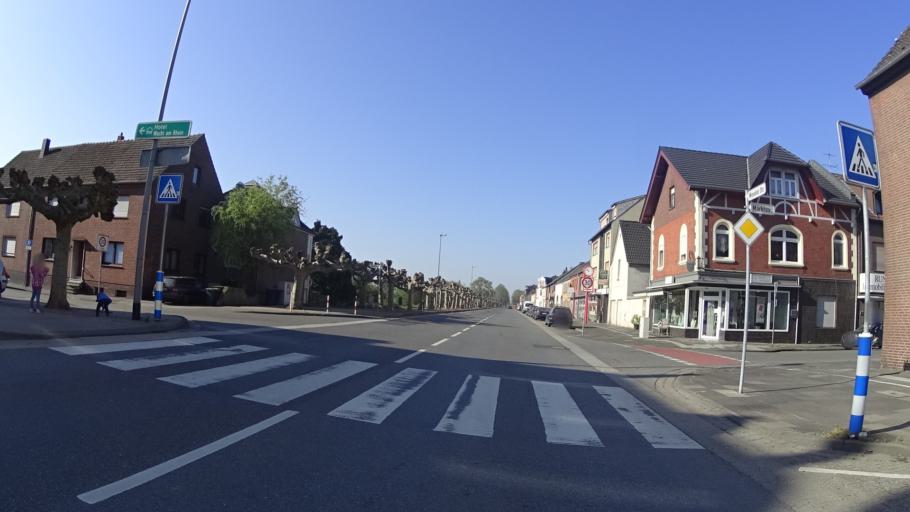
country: DE
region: North Rhine-Westphalia
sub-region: Regierungsbezirk Dusseldorf
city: Wesel
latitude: 51.6293
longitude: 6.5814
